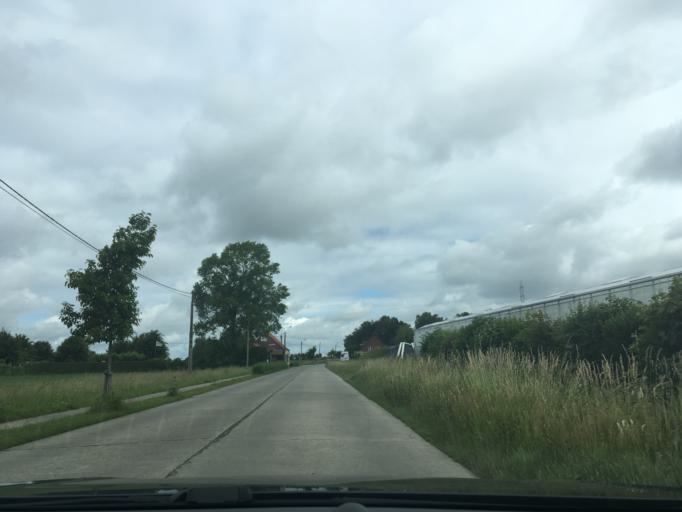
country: BE
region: Flanders
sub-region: Provincie West-Vlaanderen
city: Hooglede
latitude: 50.9547
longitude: 3.0586
